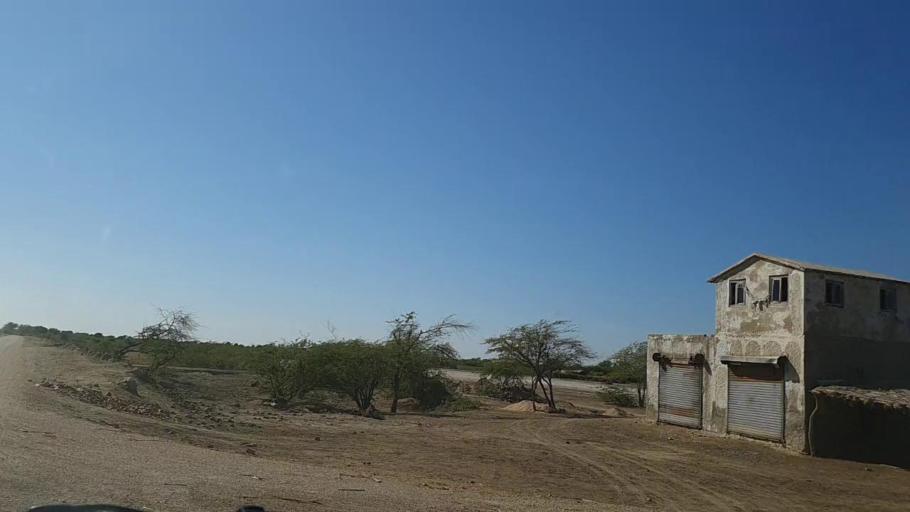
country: PK
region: Sindh
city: Dhoro Naro
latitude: 25.5271
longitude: 69.4797
